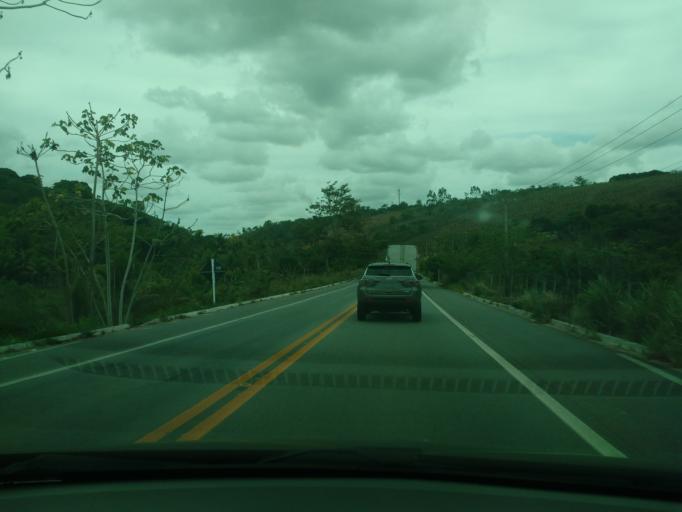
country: BR
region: Alagoas
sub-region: Uniao Dos Palmares
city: Uniao dos Palmares
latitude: -9.2374
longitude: -36.0181
